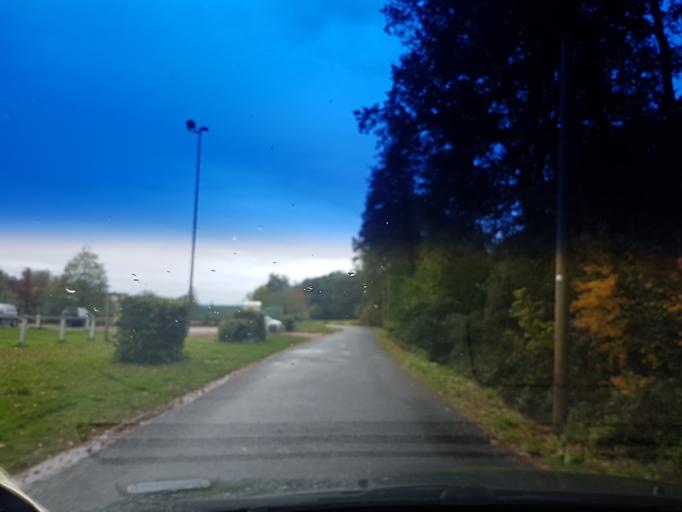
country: DE
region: Bavaria
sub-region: Regierungsbezirk Mittelfranken
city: Wachenroth
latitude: 49.7550
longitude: 10.7001
